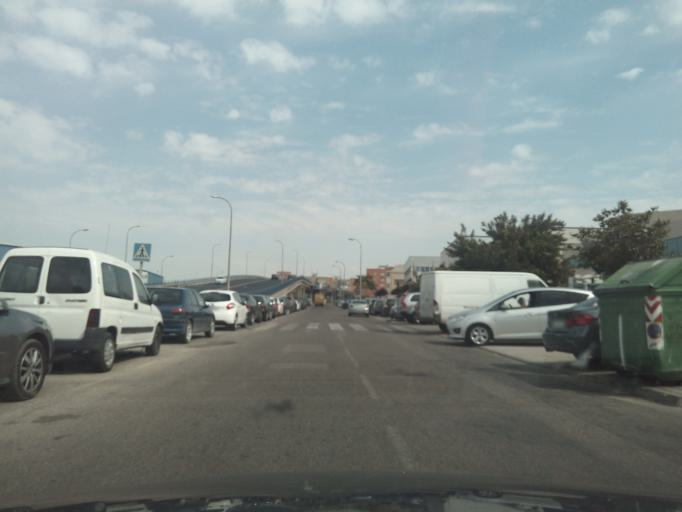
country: ES
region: Madrid
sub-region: Provincia de Madrid
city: Torrejon de Ardoz
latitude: 40.4512
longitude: -3.4831
